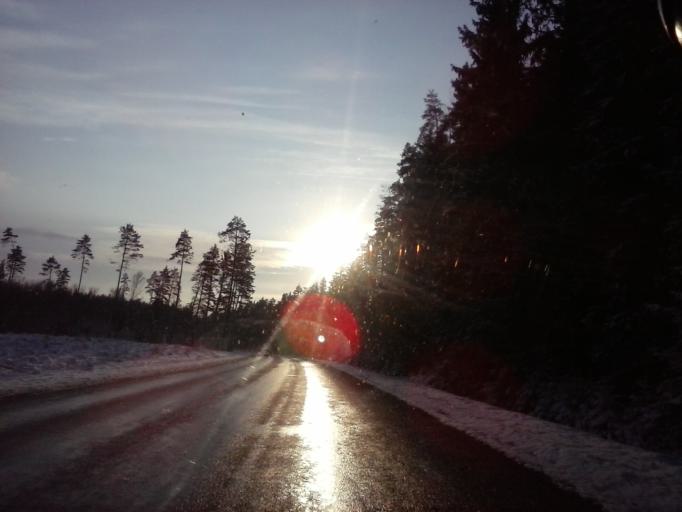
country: EE
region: Tartu
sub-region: UElenurme vald
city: Ulenurme
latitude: 58.3385
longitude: 26.8988
